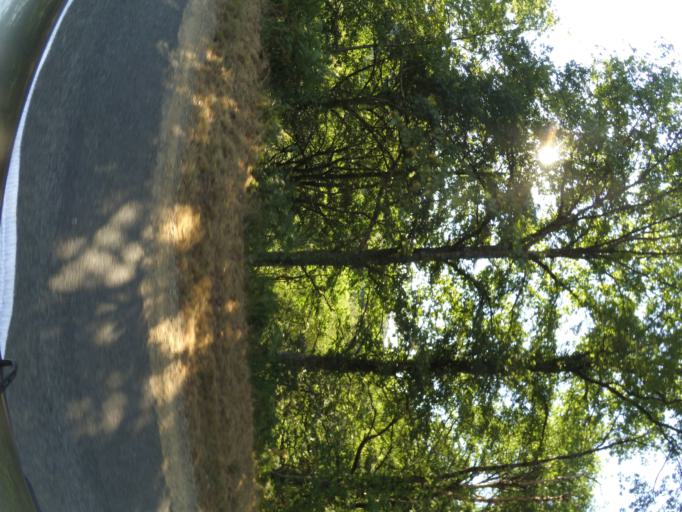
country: FR
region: Limousin
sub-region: Departement de la Haute-Vienne
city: Peyrat-le-Chateau
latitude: 45.7542
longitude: 1.8166
